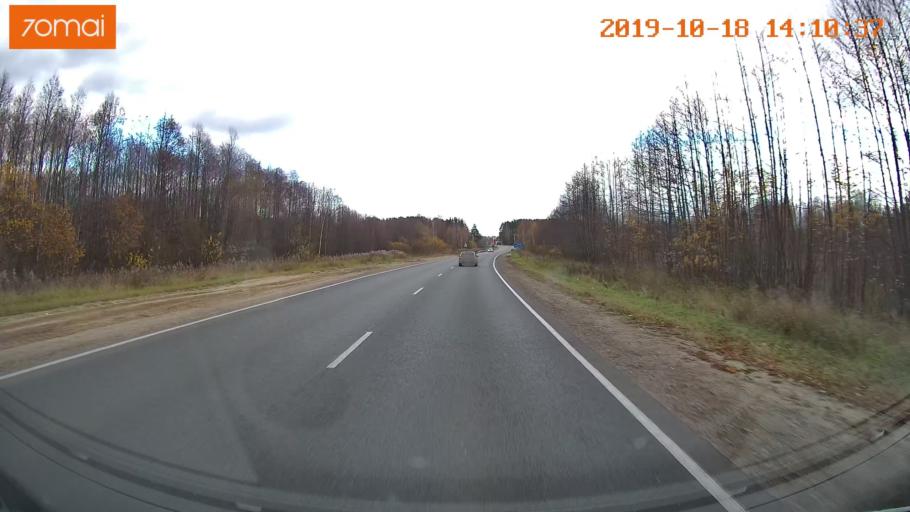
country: RU
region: Rjazan
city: Spas-Klepiki
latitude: 55.1411
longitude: 40.2121
